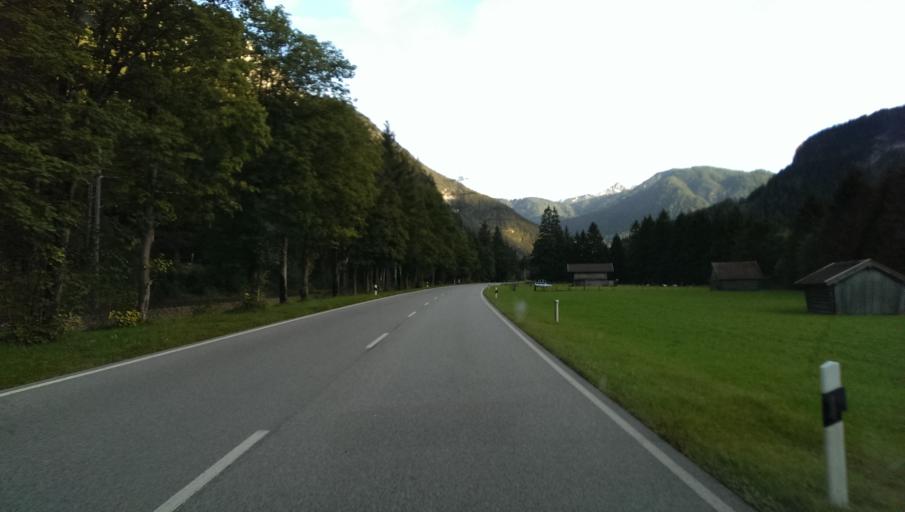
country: AT
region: Tyrol
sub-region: Politischer Bezirk Innsbruck Land
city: Scharnitz
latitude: 47.4082
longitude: 11.2604
